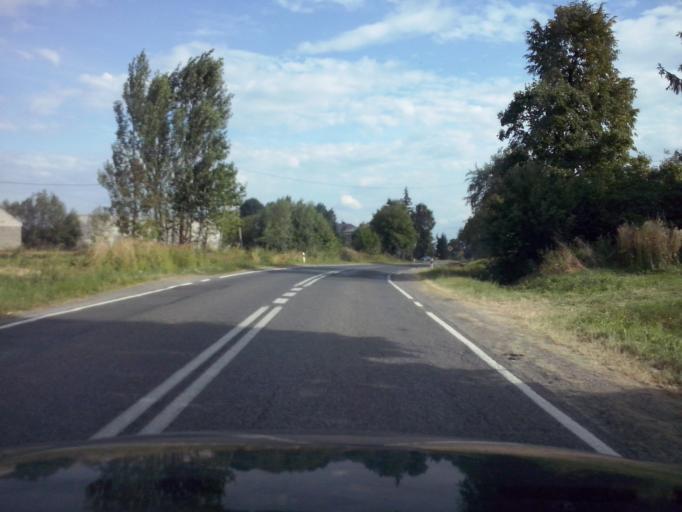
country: PL
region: Swietokrzyskie
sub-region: Powiat kielecki
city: Lagow
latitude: 50.7390
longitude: 21.0723
